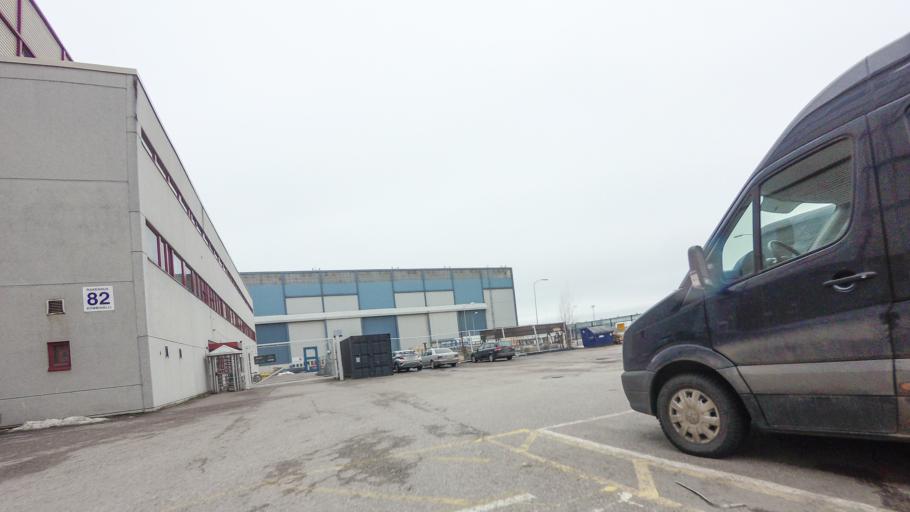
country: FI
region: Uusimaa
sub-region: Helsinki
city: Helsinki
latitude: 60.1518
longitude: 24.9252
